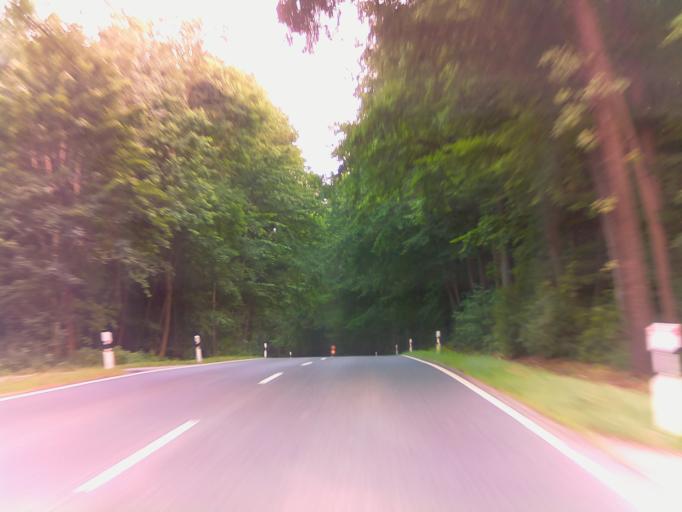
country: DE
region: Thuringia
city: Troistedt
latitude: 50.9241
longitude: 11.2531
